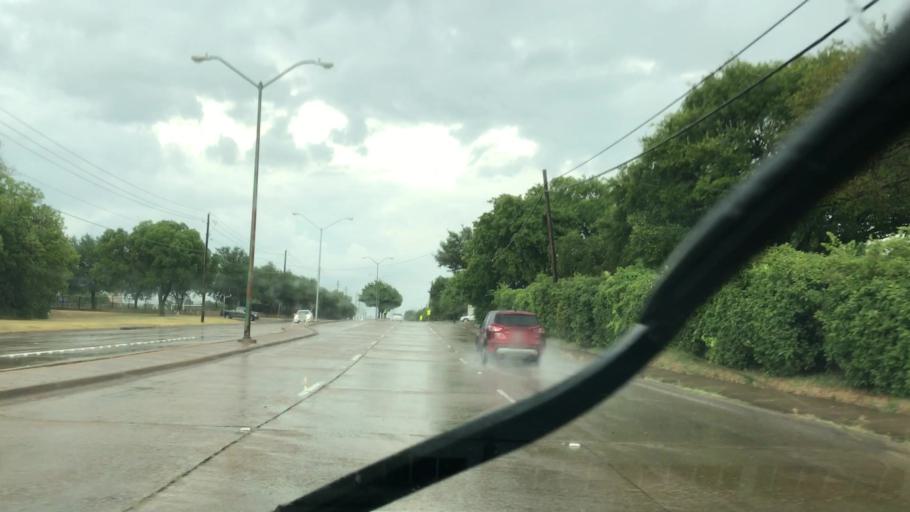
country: US
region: Texas
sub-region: Dallas County
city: Garland
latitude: 32.8788
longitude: -96.6980
